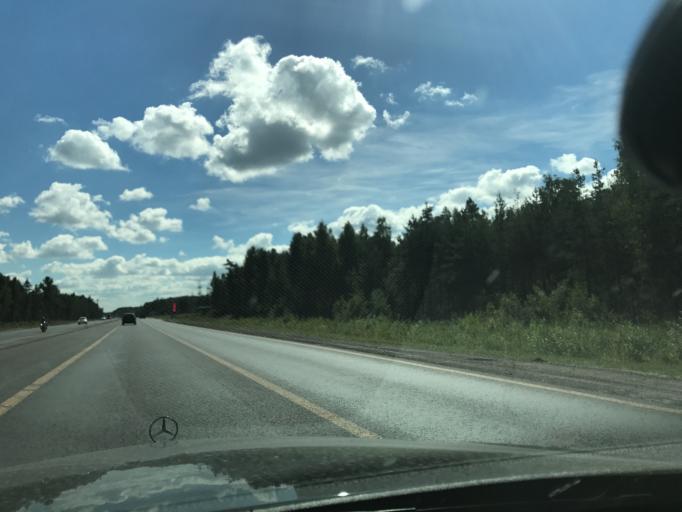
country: RU
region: Nizjnij Novgorod
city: Gorbatovka
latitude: 56.2780
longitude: 43.7010
